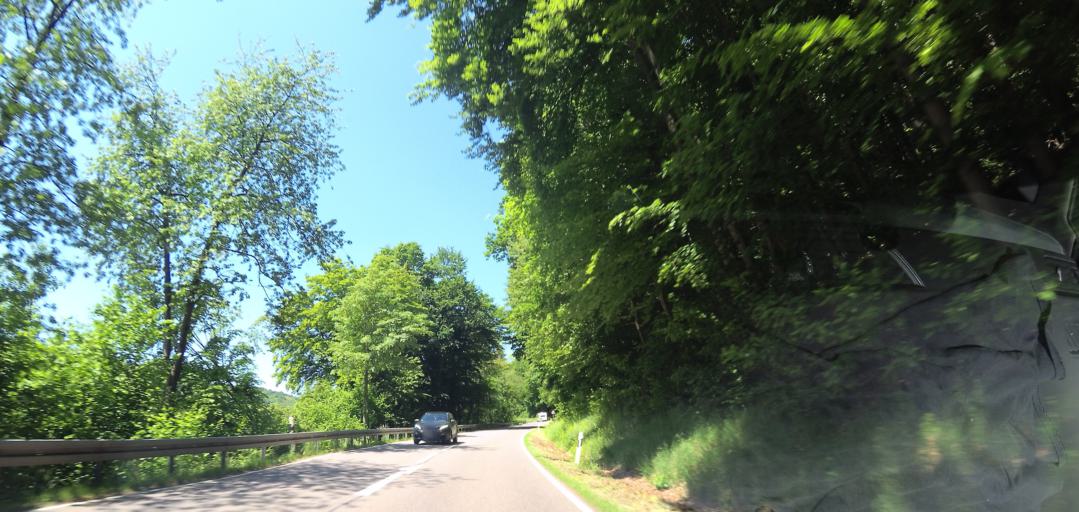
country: DE
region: Saarland
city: Losheim
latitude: 49.4564
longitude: 6.7300
